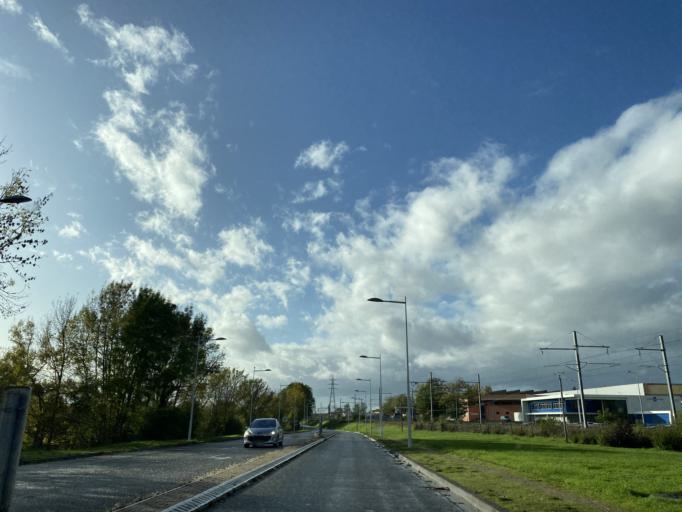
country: FR
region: Centre
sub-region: Departement du Cher
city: Saint-Doulchard
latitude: 47.0947
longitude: 2.3736
